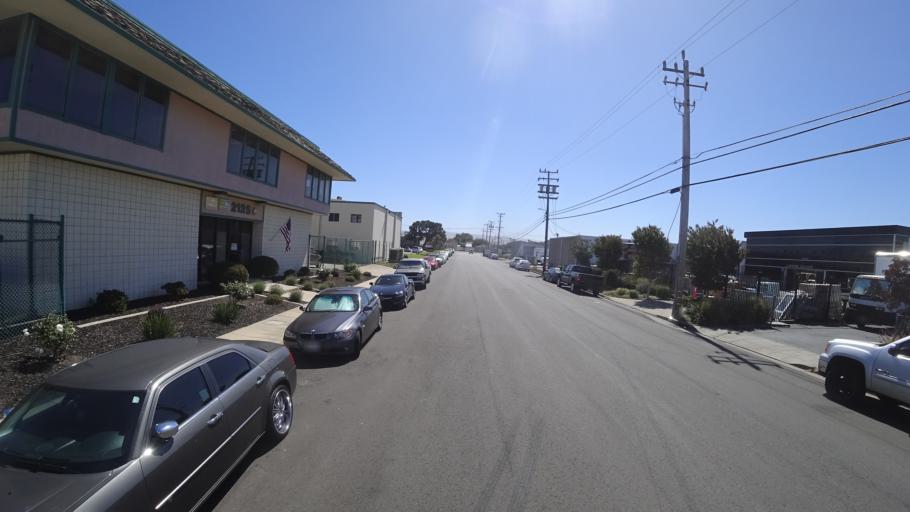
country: US
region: California
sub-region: Alameda County
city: San Lorenzo
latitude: 37.6464
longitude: -122.1221
